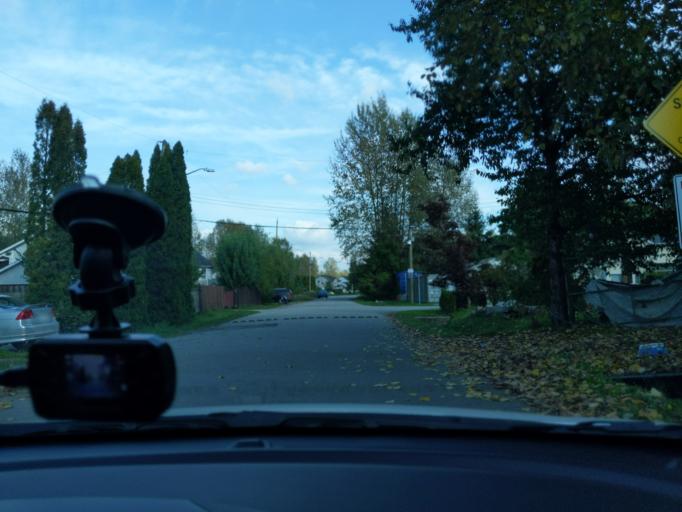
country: CA
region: British Columbia
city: Pitt Meadows
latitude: 49.2020
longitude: -122.6778
